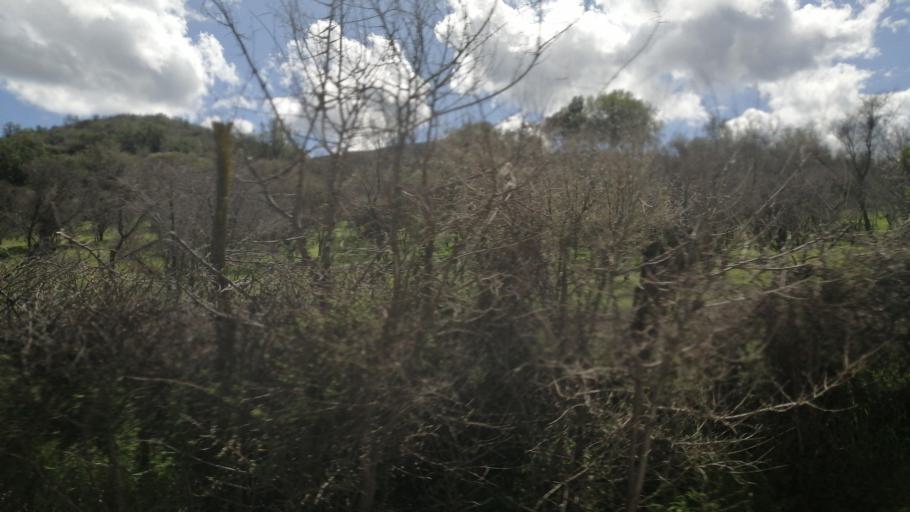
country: CL
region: Valparaiso
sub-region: Provincia de Marga Marga
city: Limache
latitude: -33.1881
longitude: -71.1959
